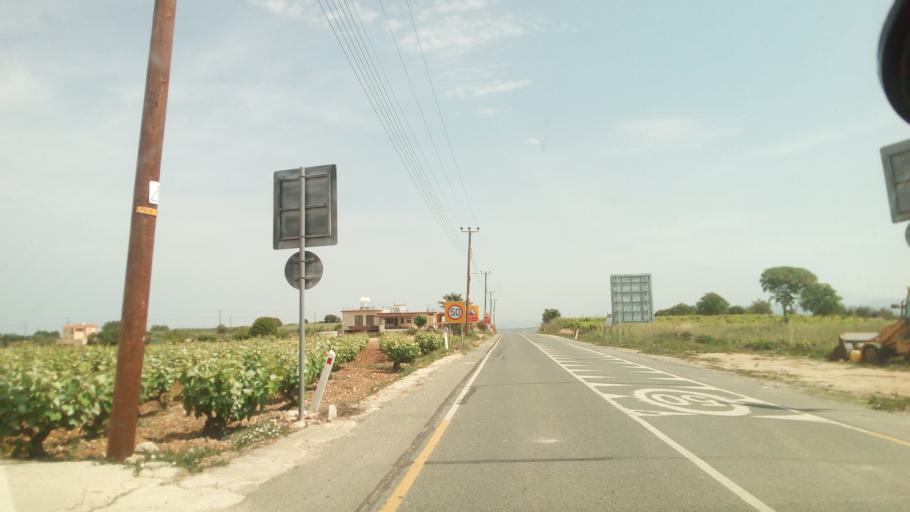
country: CY
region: Pafos
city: Mesogi
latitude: 34.8527
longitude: 32.4949
